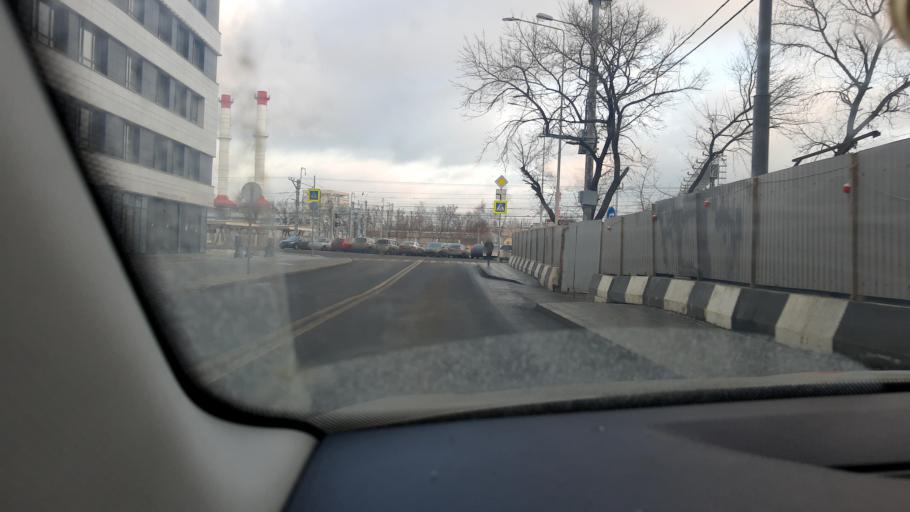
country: RU
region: Moscow
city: Tekstil'shchiki
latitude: 55.7320
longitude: 37.7329
